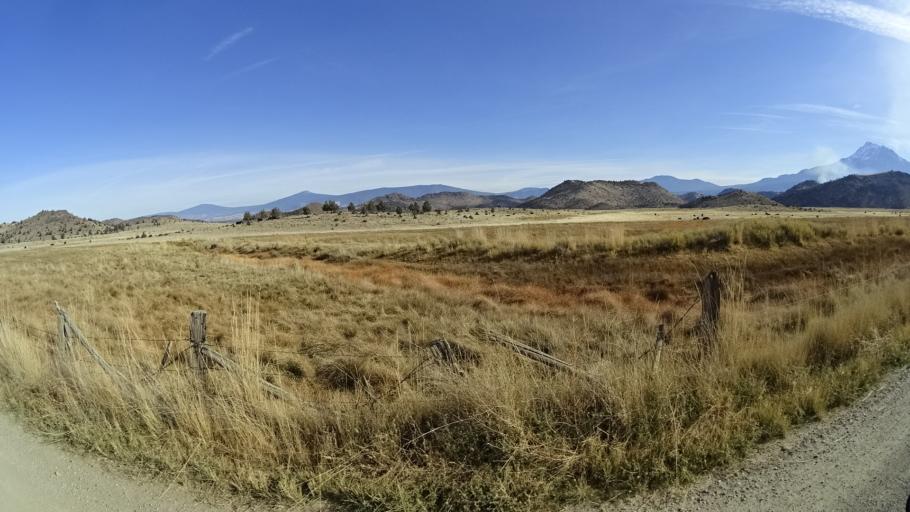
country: US
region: California
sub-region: Siskiyou County
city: Weed
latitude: 41.5366
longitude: -122.4693
